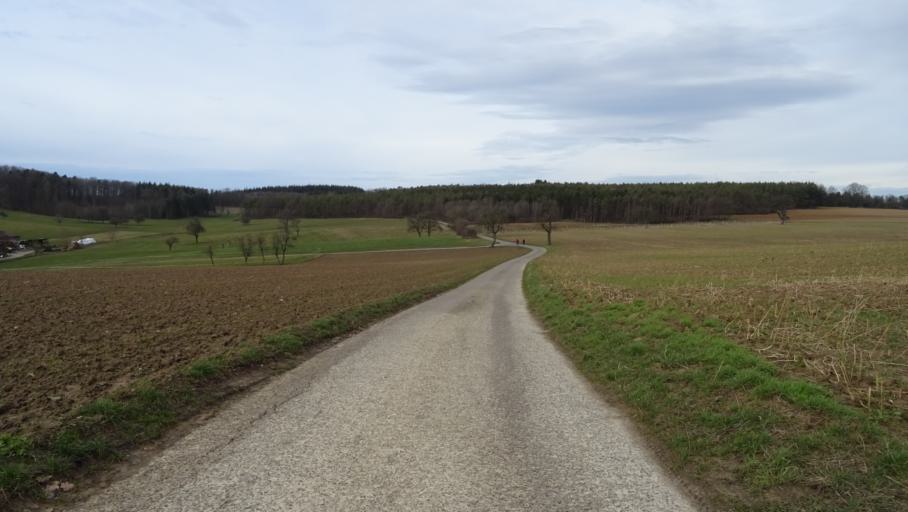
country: DE
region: Baden-Wuerttemberg
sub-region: Karlsruhe Region
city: Seckach
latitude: 49.4294
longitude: 9.2718
